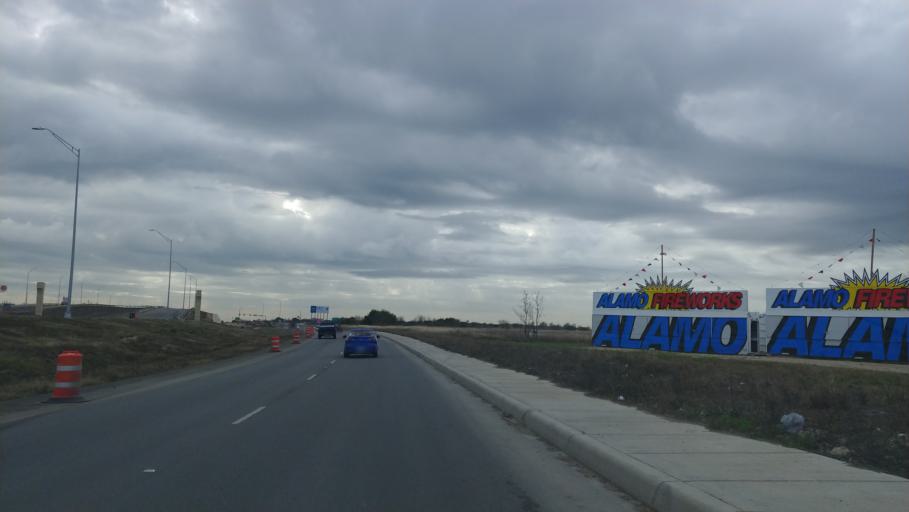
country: US
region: Texas
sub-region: Bexar County
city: Lackland Air Force Base
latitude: 29.4071
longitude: -98.7099
